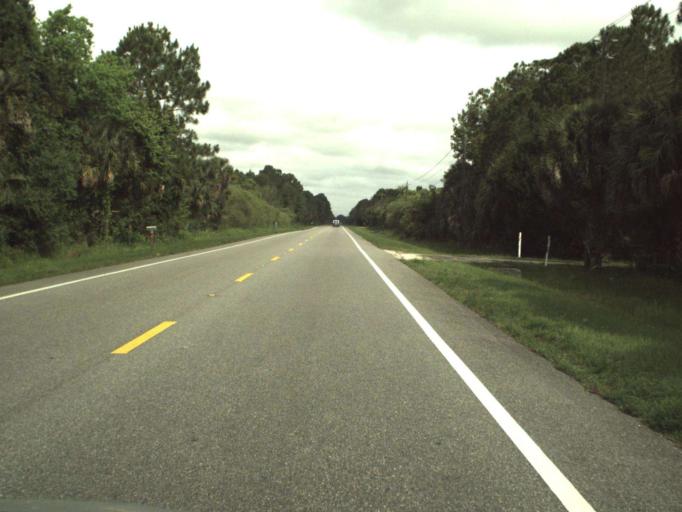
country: US
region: Florida
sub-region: Seminole County
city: Geneva
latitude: 28.7689
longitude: -81.1547
